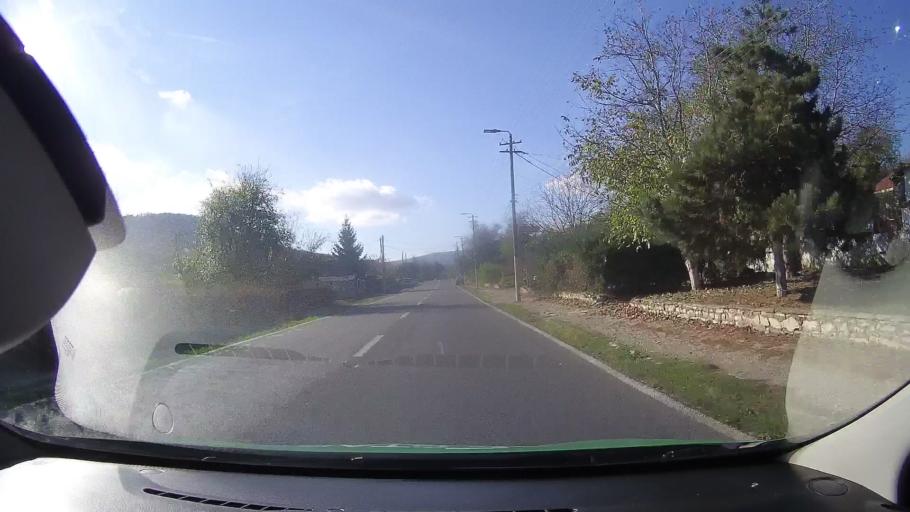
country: RO
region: Tulcea
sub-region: Oras Babadag
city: Babadag
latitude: 44.8865
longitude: 28.7040
